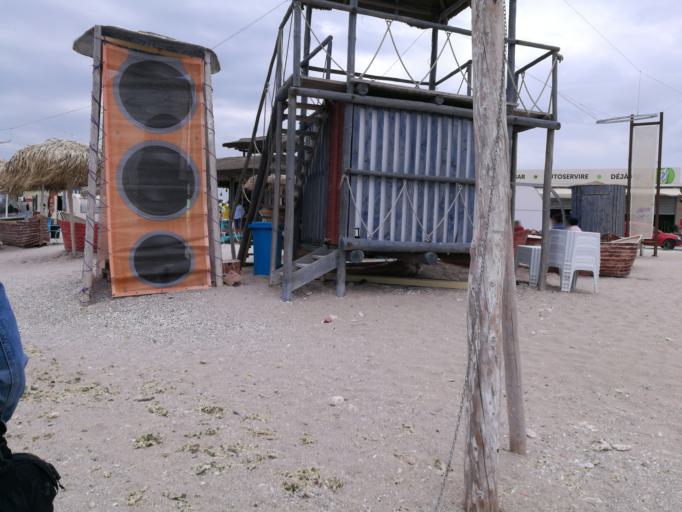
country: RO
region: Constanta
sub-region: Municipiul Mangalia
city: Mangalia
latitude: 43.7506
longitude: 28.5772
